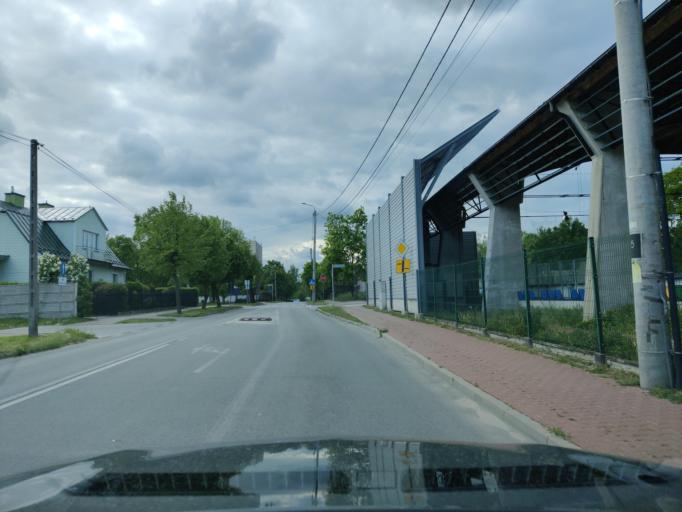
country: PL
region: Swietokrzyskie
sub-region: Powiat skarzyski
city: Skarzysko-Kamienna
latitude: 51.1189
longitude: 20.8596
